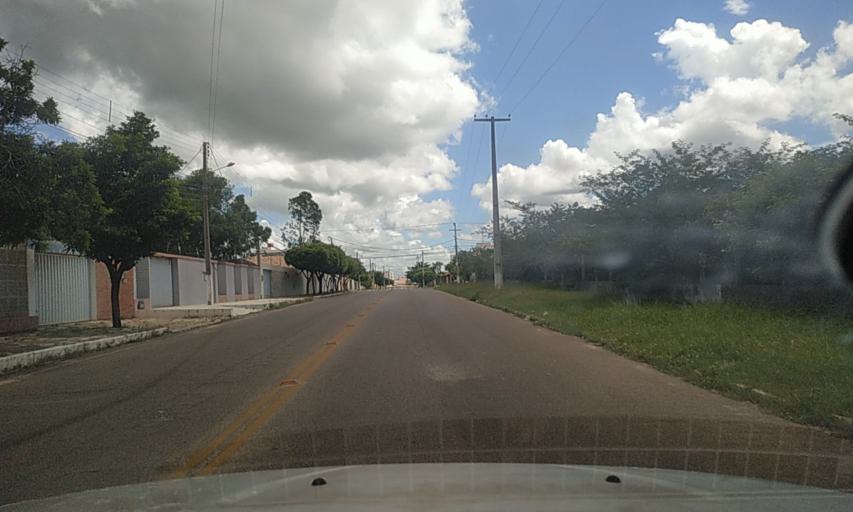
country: BR
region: Rio Grande do Norte
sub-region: Mossoro
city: Mossoro
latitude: -5.1787
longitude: -37.3626
